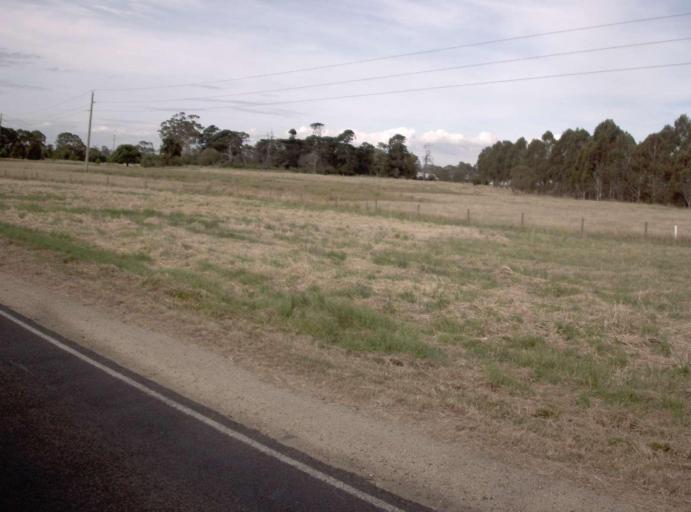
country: AU
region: Victoria
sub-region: Wellington
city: Heyfield
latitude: -38.0045
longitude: 146.7806
